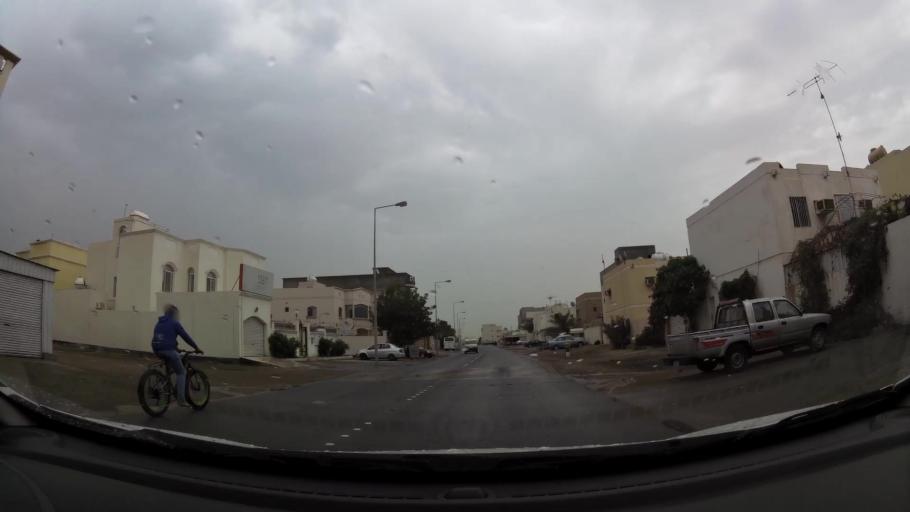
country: BH
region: Northern
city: Madinat `Isa
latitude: 26.1607
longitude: 50.5739
